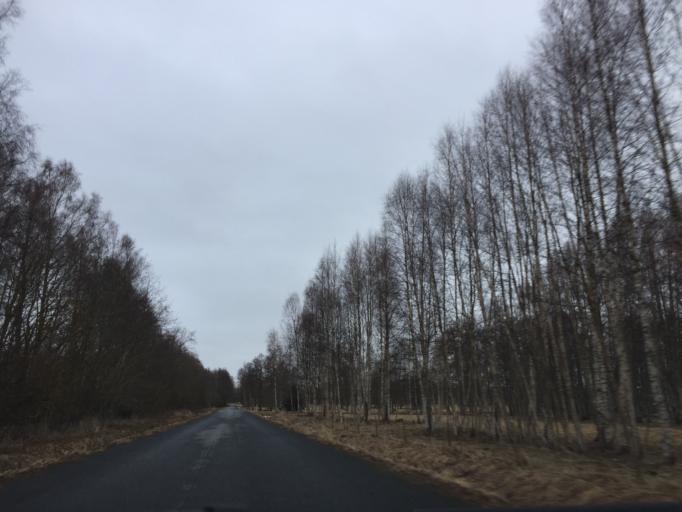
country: EE
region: Laeaene
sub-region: Haapsalu linn
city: Haapsalu
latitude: 58.7885
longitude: 23.4791
